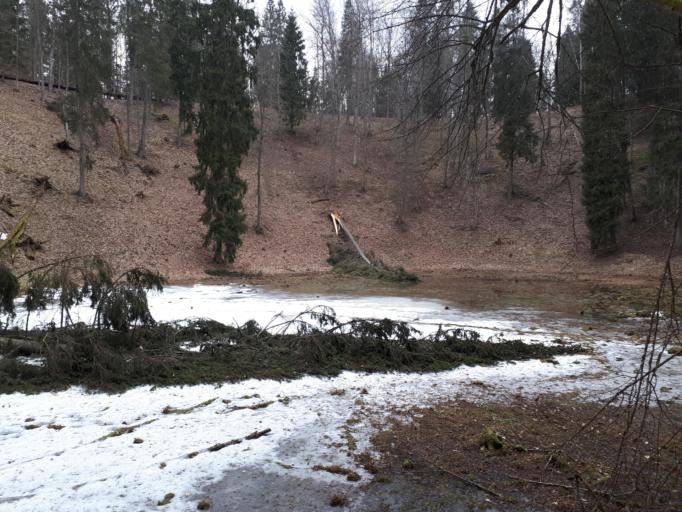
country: LT
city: Aukstadvaris
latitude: 54.6117
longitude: 24.5156
